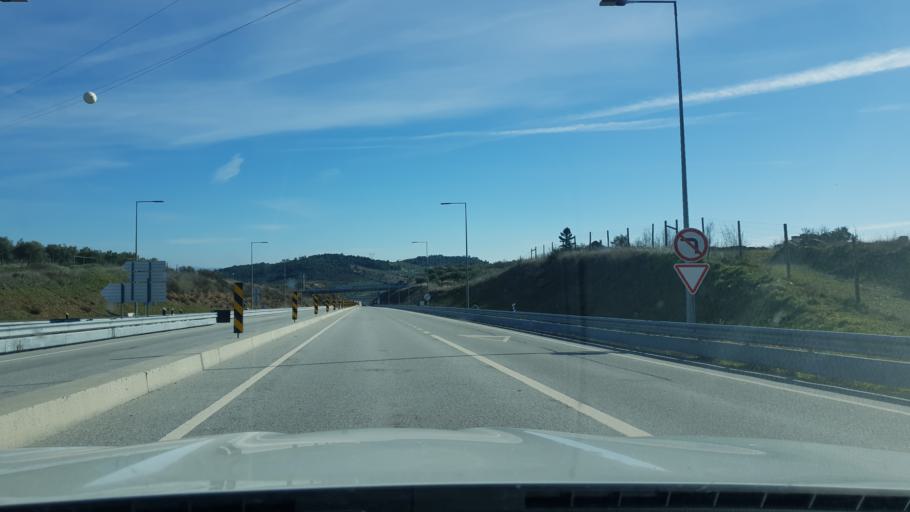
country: PT
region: Braganca
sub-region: Braganca Municipality
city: Vila Flor
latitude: 41.3011
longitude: -7.1545
